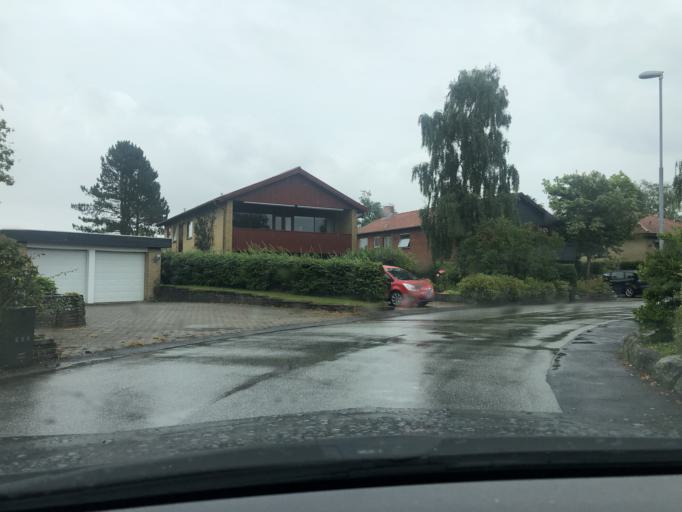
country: DK
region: South Denmark
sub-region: Vejle Kommune
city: Vejle
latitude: 55.7659
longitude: 9.5477
